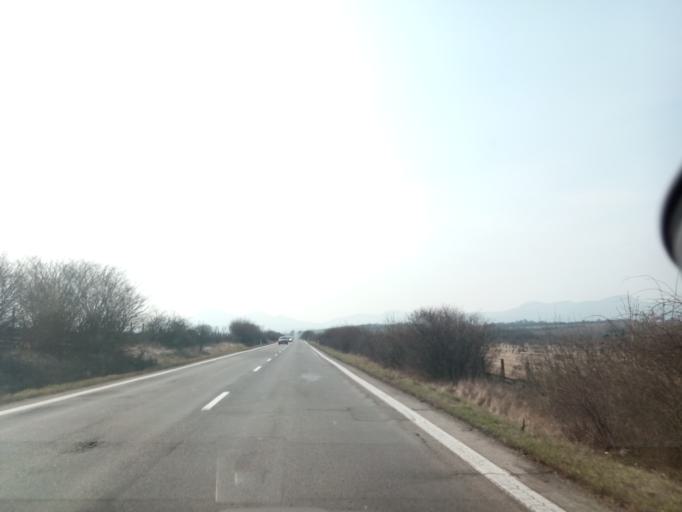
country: HU
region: Borsod-Abauj-Zemplen
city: Satoraljaujhely
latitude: 48.4998
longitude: 21.6521
